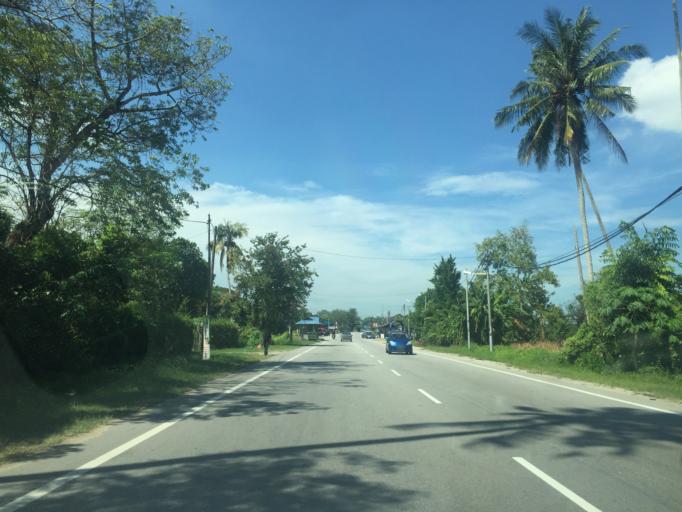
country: MY
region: Penang
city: Tasek Glugor
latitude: 5.4880
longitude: 100.4737
